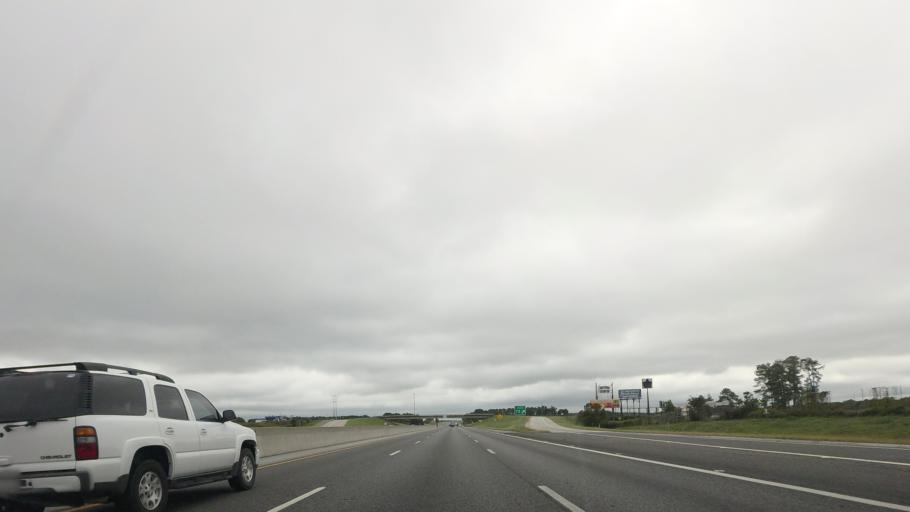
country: US
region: Georgia
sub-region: Turner County
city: Ashburn
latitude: 31.6288
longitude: -83.5783
